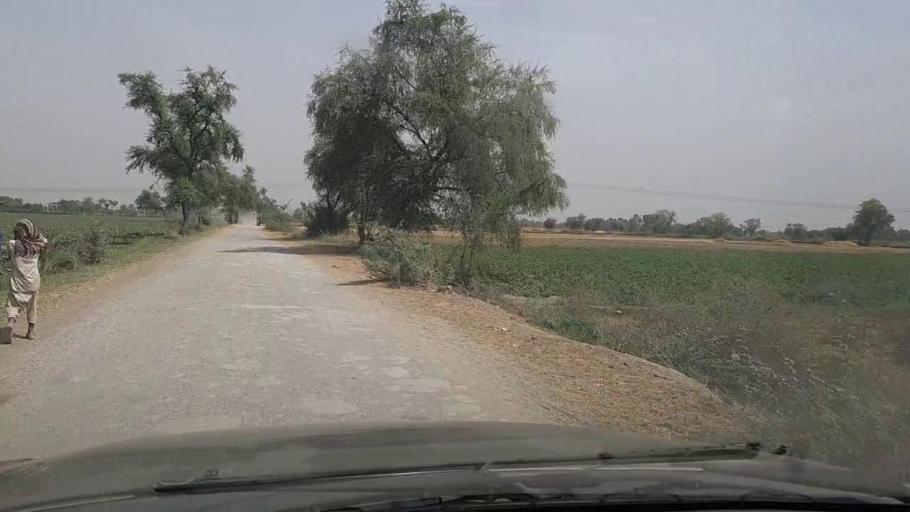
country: PK
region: Sindh
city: Shikarpur
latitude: 27.9213
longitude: 68.6759
